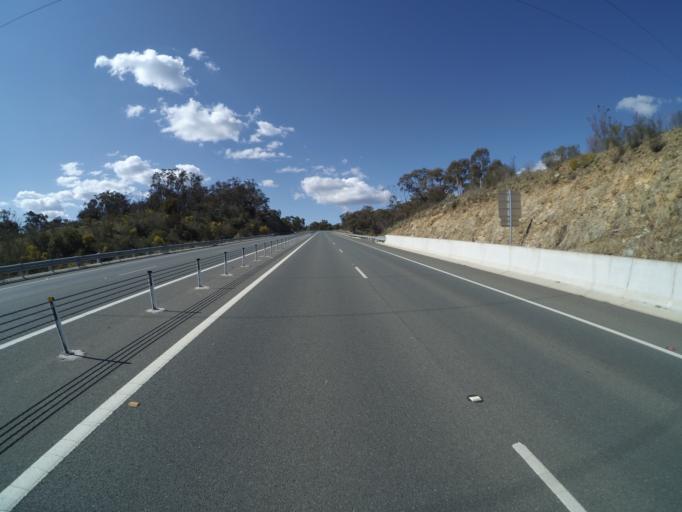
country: AU
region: New South Wales
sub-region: Queanbeyan
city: Queanbeyan
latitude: -35.3431
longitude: 149.2519
